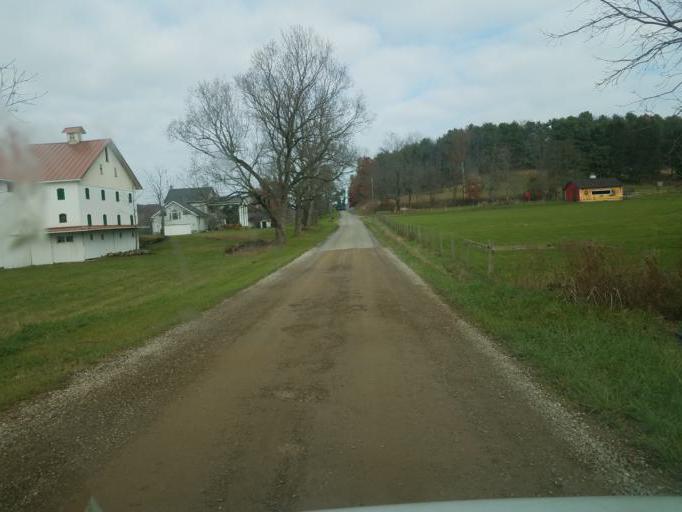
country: US
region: Ohio
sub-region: Knox County
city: Danville
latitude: 40.5220
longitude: -82.2852
